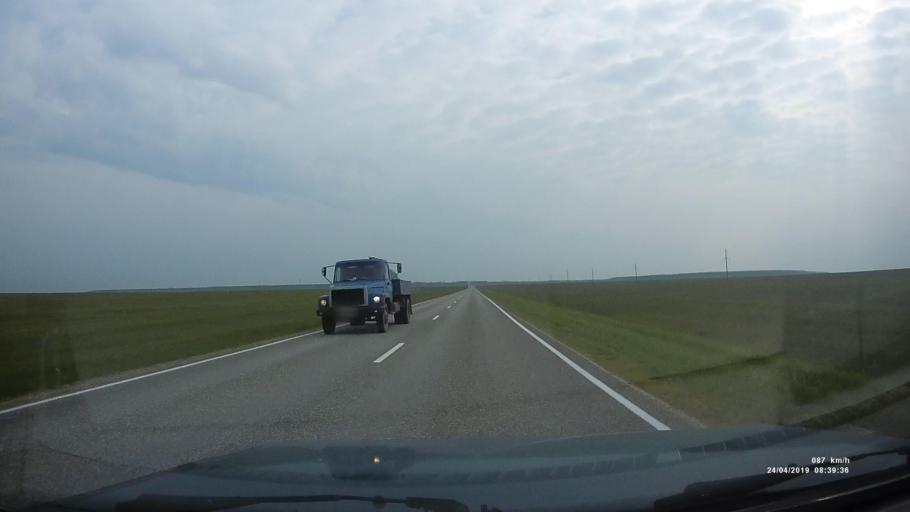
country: RU
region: Kalmykiya
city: Arshan'
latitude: 46.2218
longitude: 43.9869
